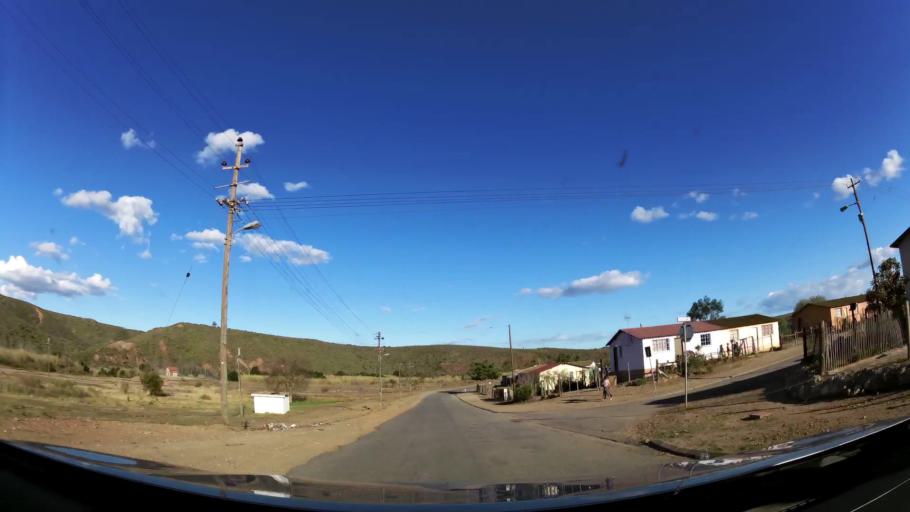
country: ZA
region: Western Cape
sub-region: Eden District Municipality
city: Riversdale
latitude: -34.1029
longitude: 20.9694
